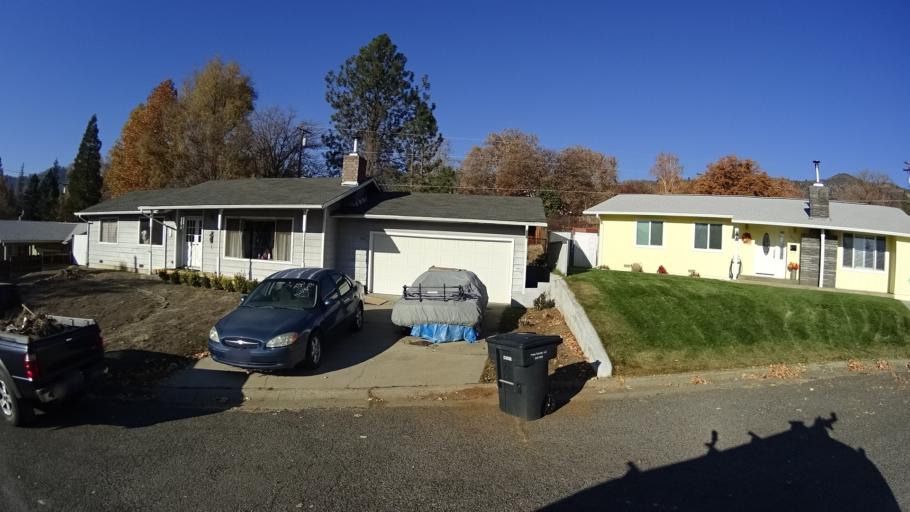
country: US
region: California
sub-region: Siskiyou County
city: Yreka
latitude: 41.7412
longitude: -122.6476
